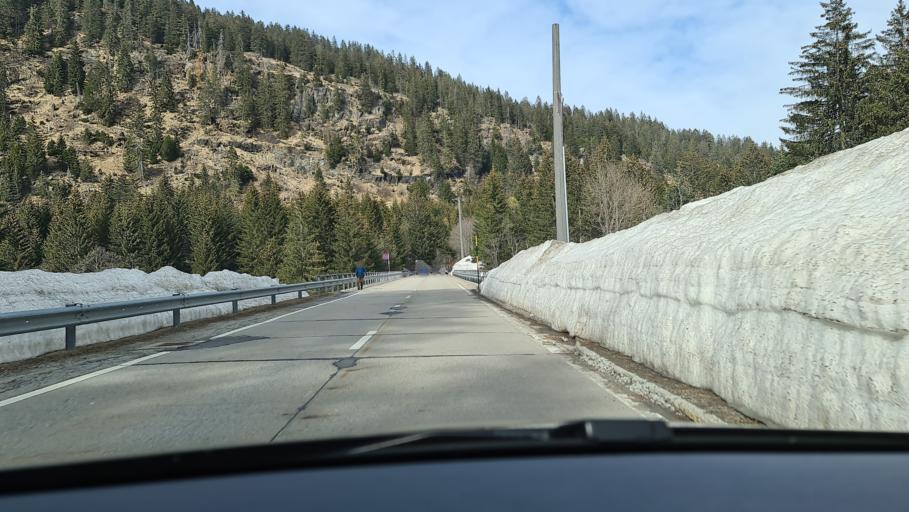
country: CH
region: Ticino
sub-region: Blenio District
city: Cancori
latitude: 46.5204
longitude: 8.8837
